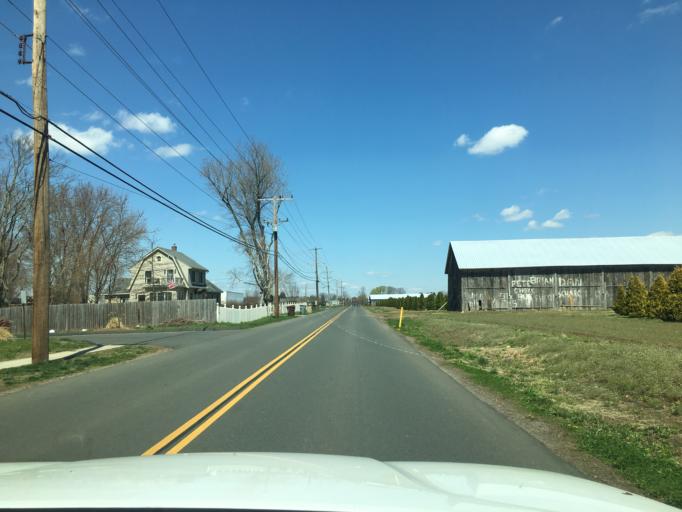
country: US
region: Connecticut
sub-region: Hartford County
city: Hazardville
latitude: 41.9872
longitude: -72.5280
